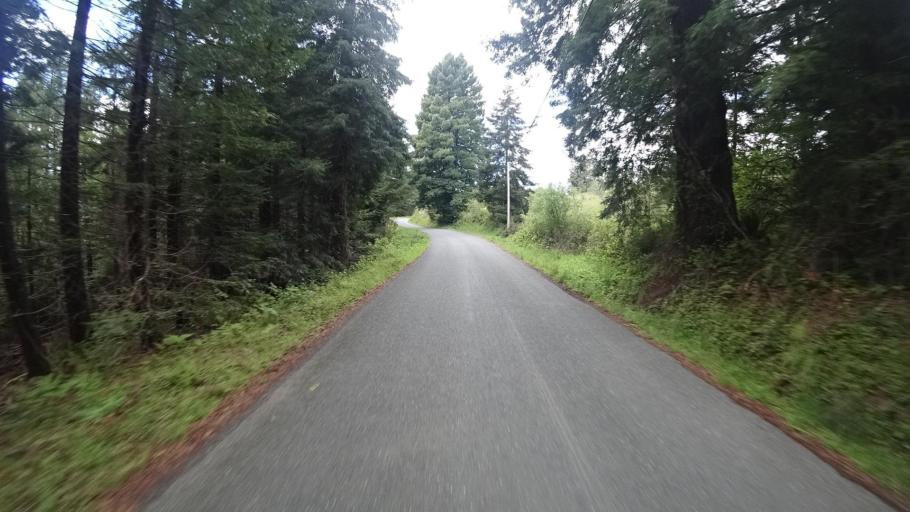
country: US
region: California
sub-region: Humboldt County
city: Blue Lake
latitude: 40.8567
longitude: -123.9328
